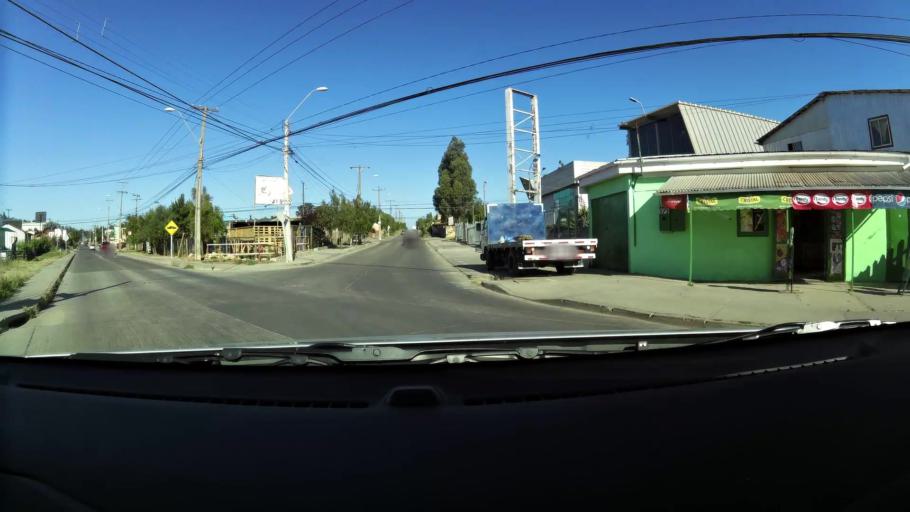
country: CL
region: Valparaiso
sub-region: Provincia de Valparaiso
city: Vina del Mar
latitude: -33.1156
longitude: -71.5674
